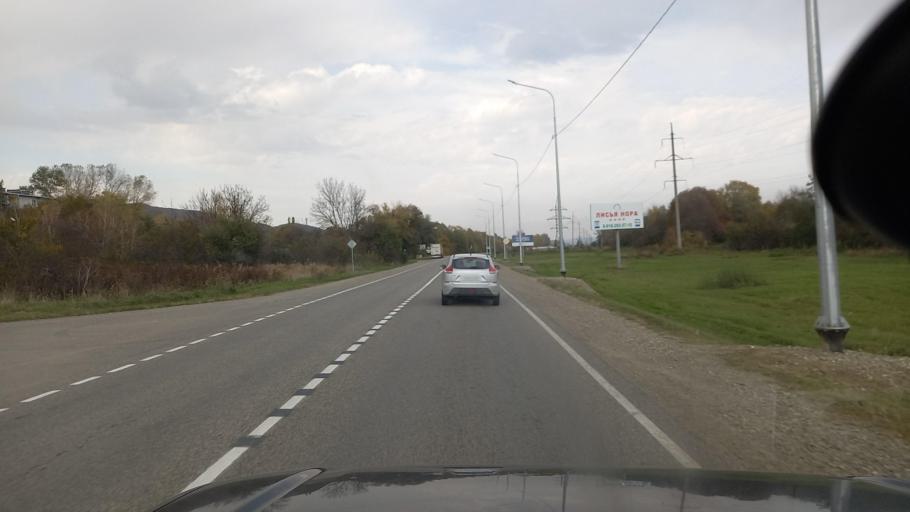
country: RU
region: Krasnodarskiy
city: Shedok
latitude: 44.1782
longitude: 40.8412
